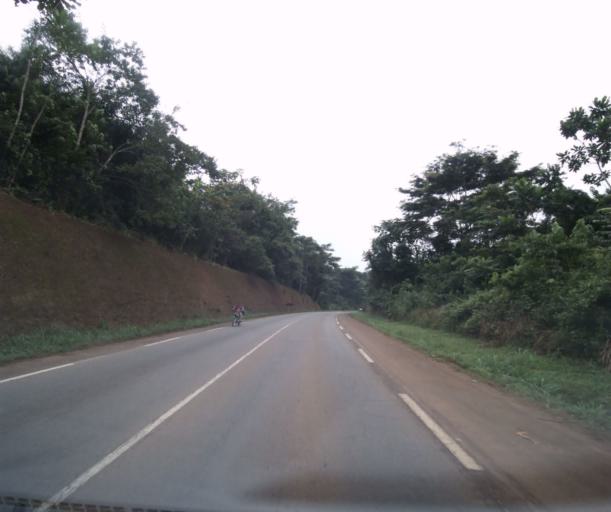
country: CM
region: Centre
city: Mbankomo
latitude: 3.7605
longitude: 11.1032
